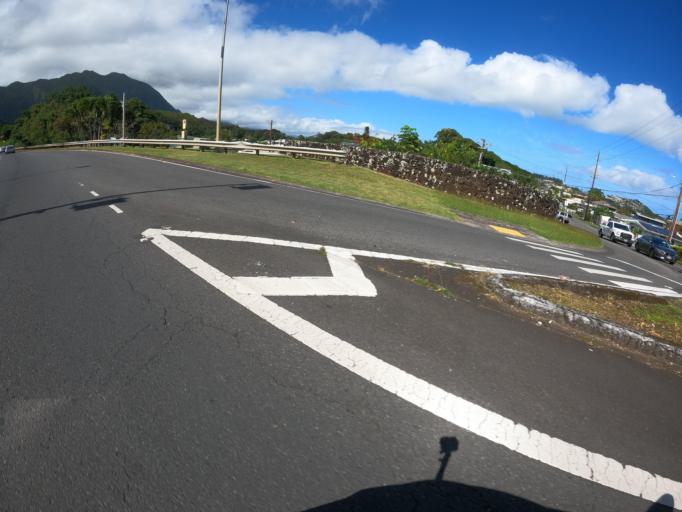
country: US
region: Hawaii
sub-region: Honolulu County
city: Kane'ohe
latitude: 21.4039
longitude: -157.8035
